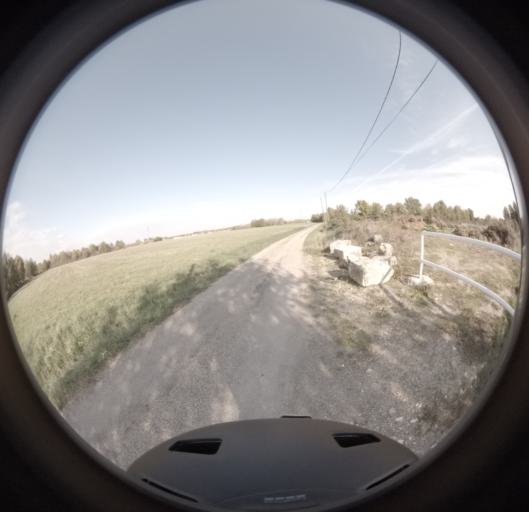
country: FR
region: Midi-Pyrenees
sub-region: Departement du Tarn-et-Garonne
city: Montbeton
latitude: 43.9917
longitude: 1.2733
